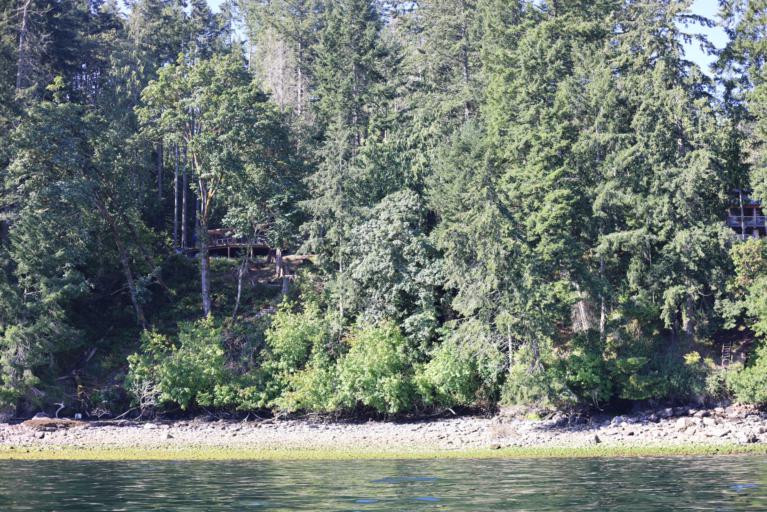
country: CA
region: British Columbia
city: North Cowichan
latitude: 48.8035
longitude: -123.5754
